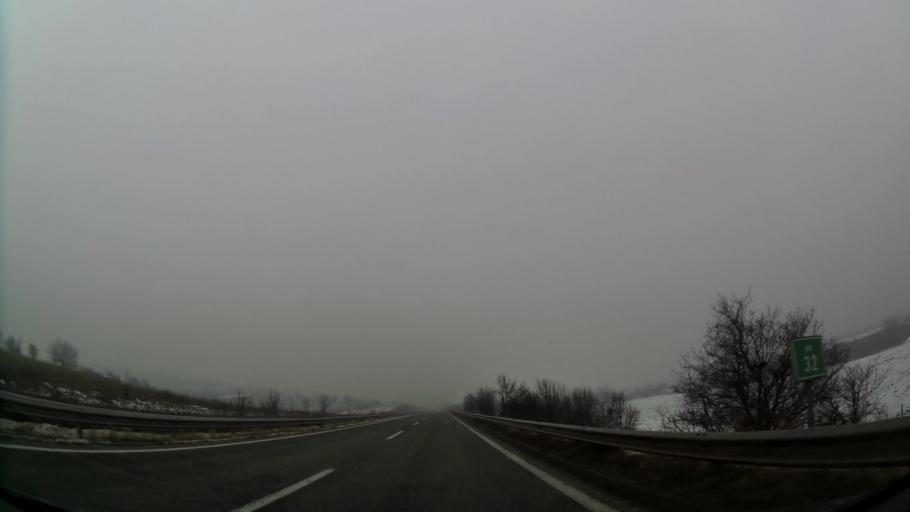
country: MK
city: Miladinovci
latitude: 41.9678
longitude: 21.6425
